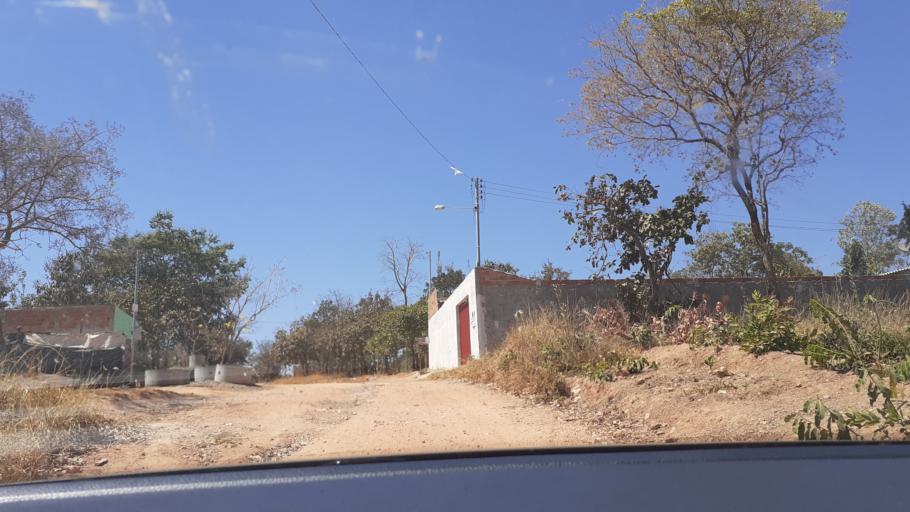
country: BR
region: Goias
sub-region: Caldas Novas
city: Caldas Novas
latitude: -17.7406
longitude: -48.6509
